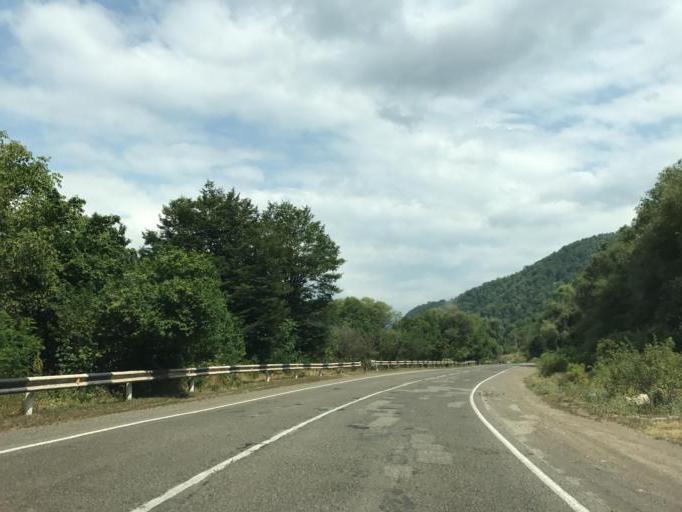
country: AM
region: Tavush
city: Haghartsin
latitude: 40.7760
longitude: 44.9408
